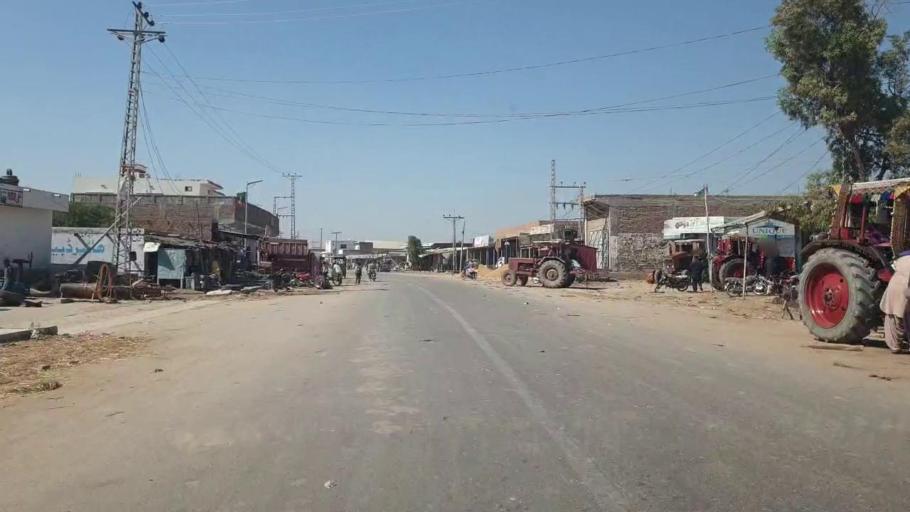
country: PK
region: Sindh
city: Talhar
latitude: 24.8858
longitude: 68.8075
